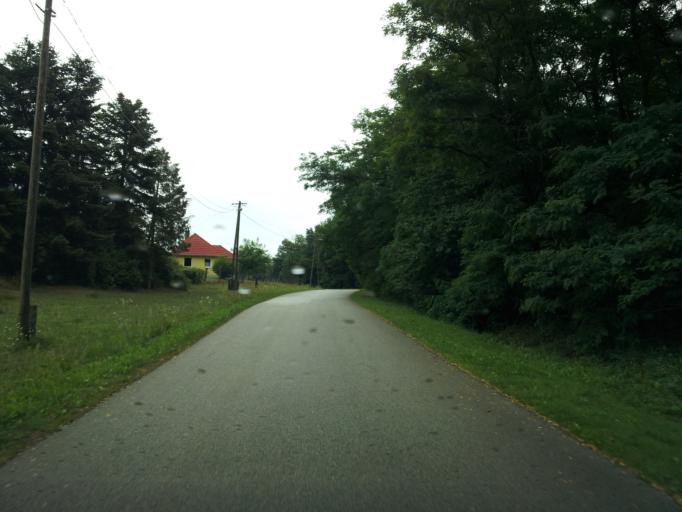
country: HU
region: Vas
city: Kormend
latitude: 46.9606
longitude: 16.6091
